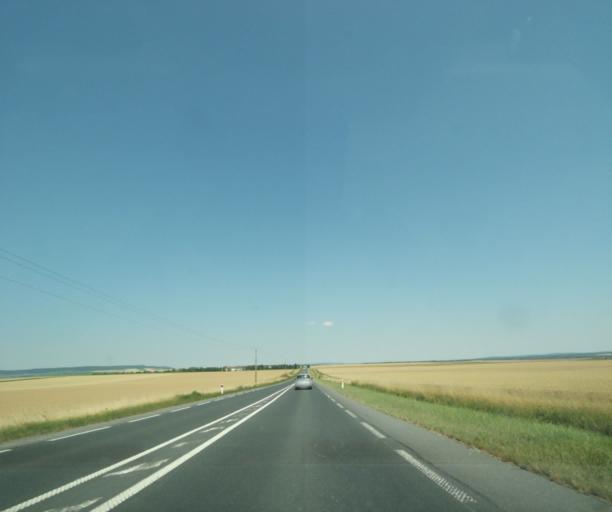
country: FR
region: Champagne-Ardenne
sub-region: Departement de la Marne
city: Mourmelon-le-Grand
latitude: 49.0780
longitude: 4.2848
